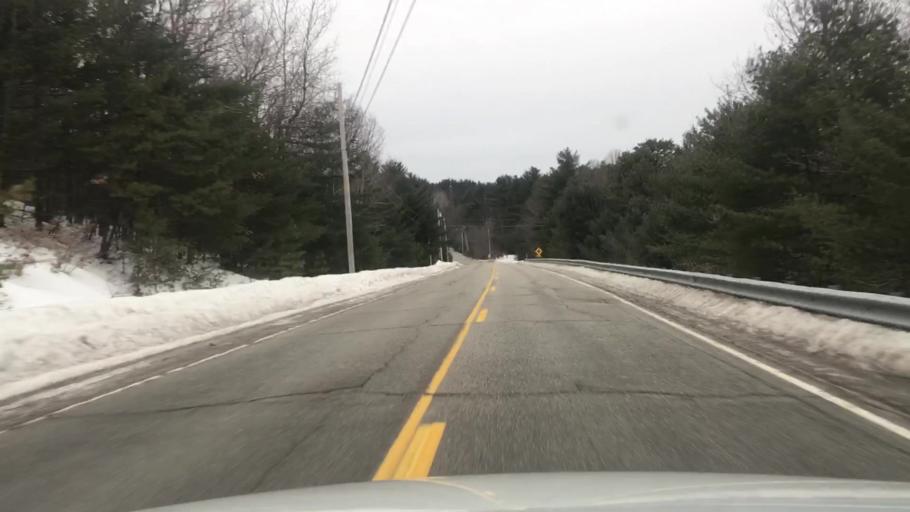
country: US
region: Maine
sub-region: York County
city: Newfield
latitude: 43.6001
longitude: -70.8830
